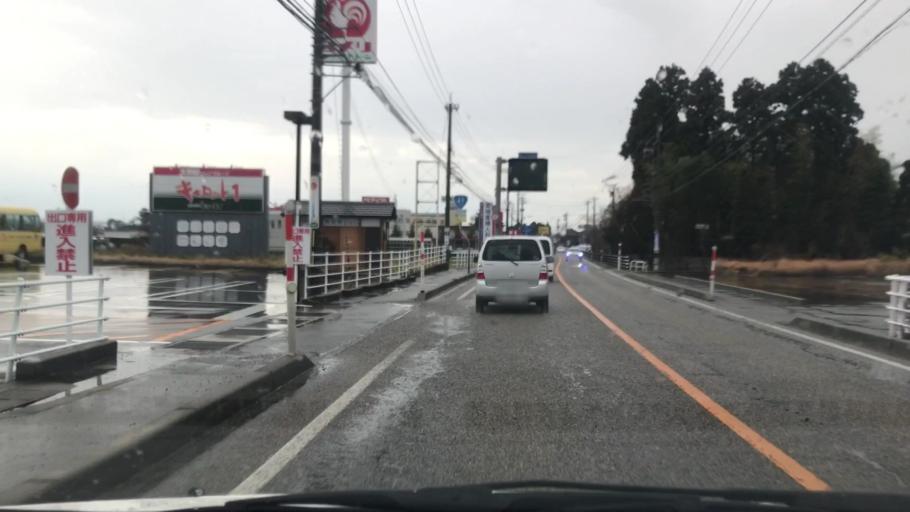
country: JP
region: Toyama
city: Yatsuomachi-higashikumisaka
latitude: 36.6064
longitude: 137.2038
